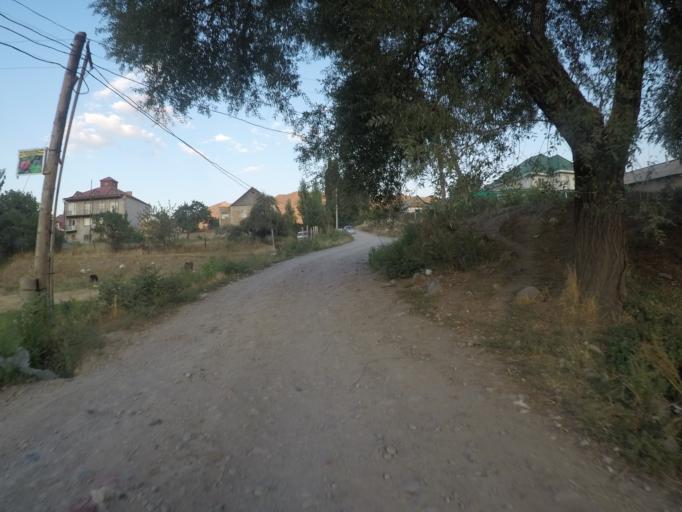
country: KG
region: Chuy
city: Bishkek
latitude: 42.7795
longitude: 74.6477
